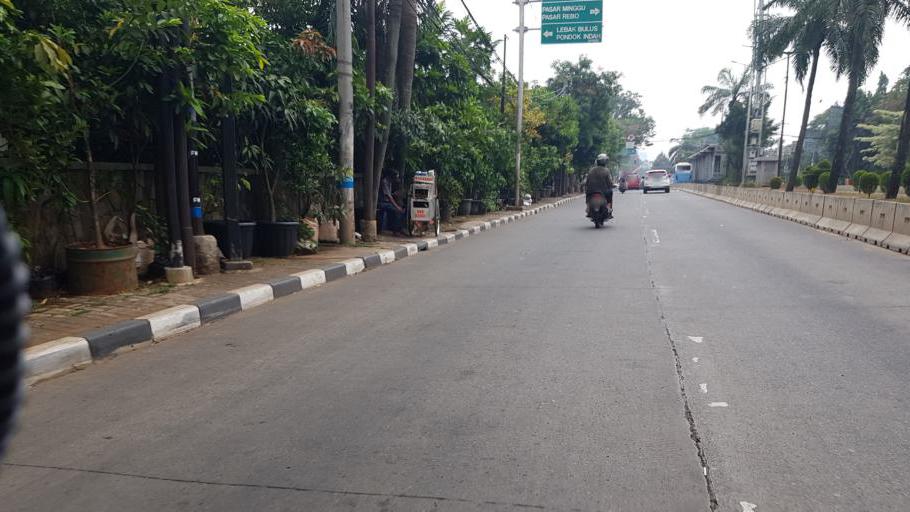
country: ID
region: Jakarta Raya
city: Jakarta
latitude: -6.2956
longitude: 106.8216
